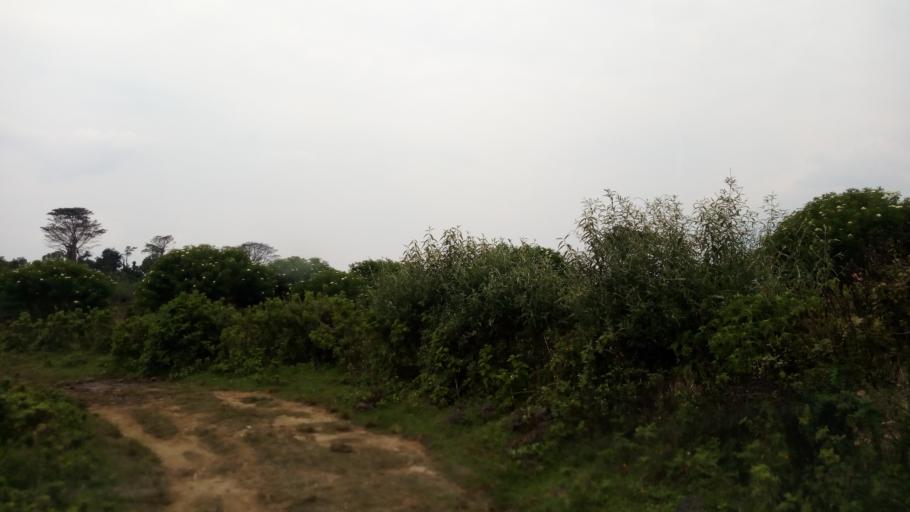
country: UG
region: Western Region
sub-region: Kisoro District
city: Kisoro
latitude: -1.2654
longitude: 29.6077
